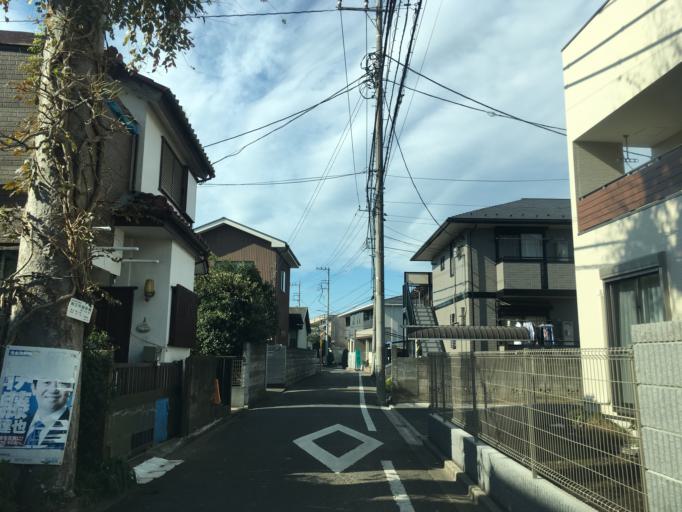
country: JP
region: Tokyo
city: Chofugaoka
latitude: 35.6283
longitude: 139.5818
